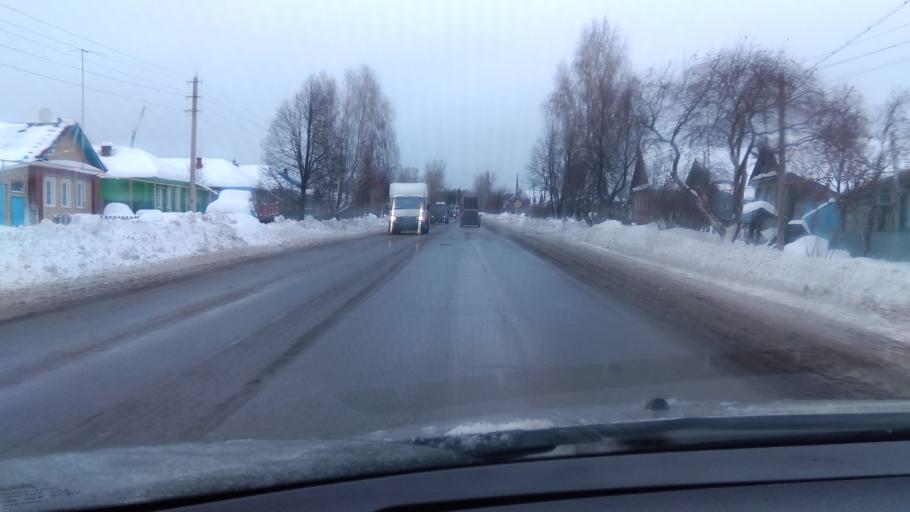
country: RU
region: Sverdlovsk
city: Nikolo-Pavlovskoye
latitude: 57.7905
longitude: 60.0558
